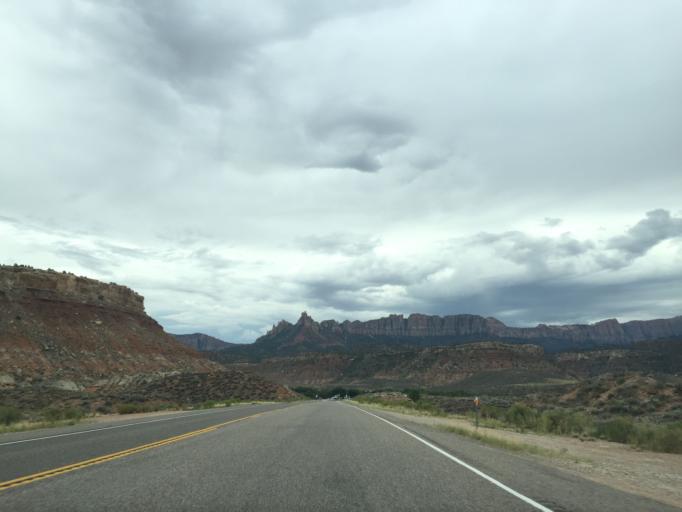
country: US
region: Utah
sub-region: Washington County
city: Hildale
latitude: 37.1679
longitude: -113.0648
